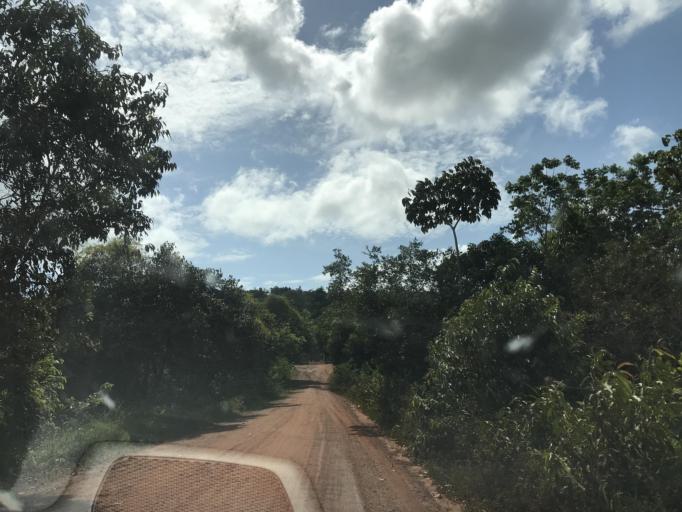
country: BR
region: Bahia
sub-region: Entre Rios
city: Entre Rios
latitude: -12.1619
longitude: -38.0762
